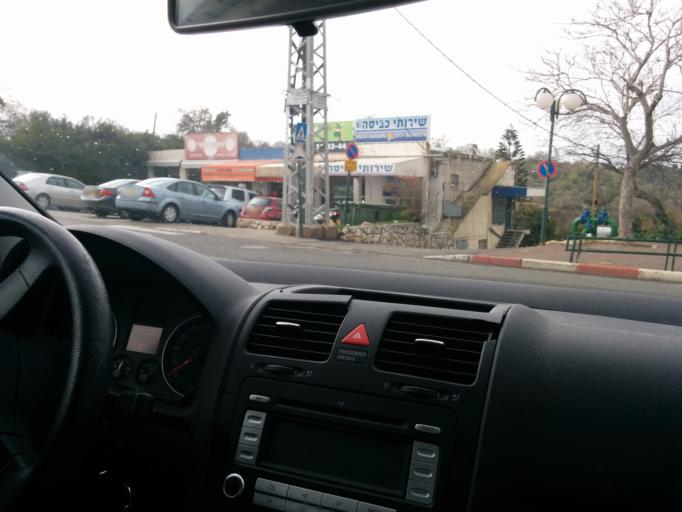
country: IL
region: Northern District
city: Basmat Tab`un
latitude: 32.7271
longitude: 35.1401
